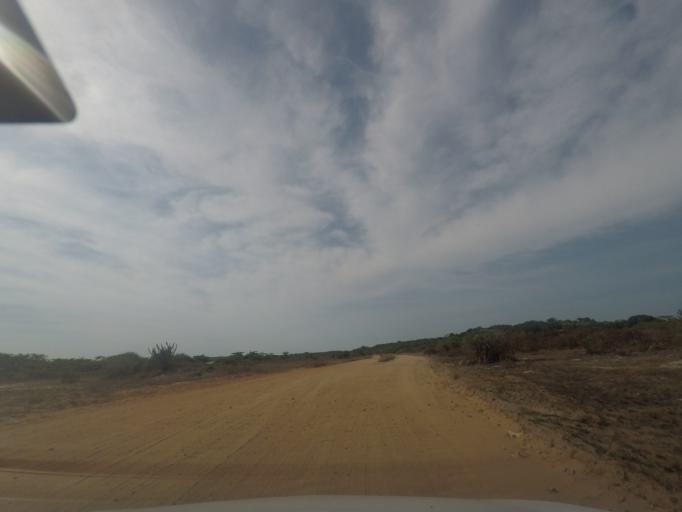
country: BR
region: Rio de Janeiro
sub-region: Marica
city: Marica
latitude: -22.9502
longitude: -42.8861
